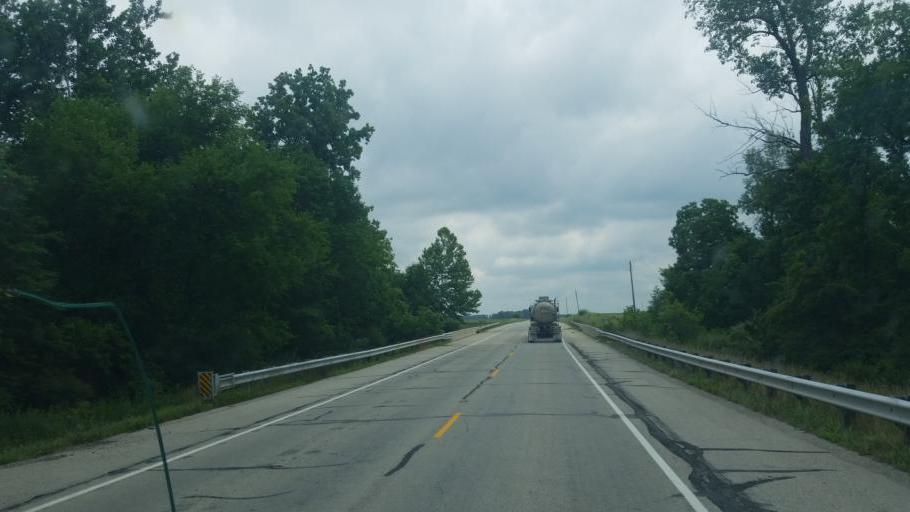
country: US
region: Indiana
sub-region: Huntington County
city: Warren
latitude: 40.6540
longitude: -85.3910
